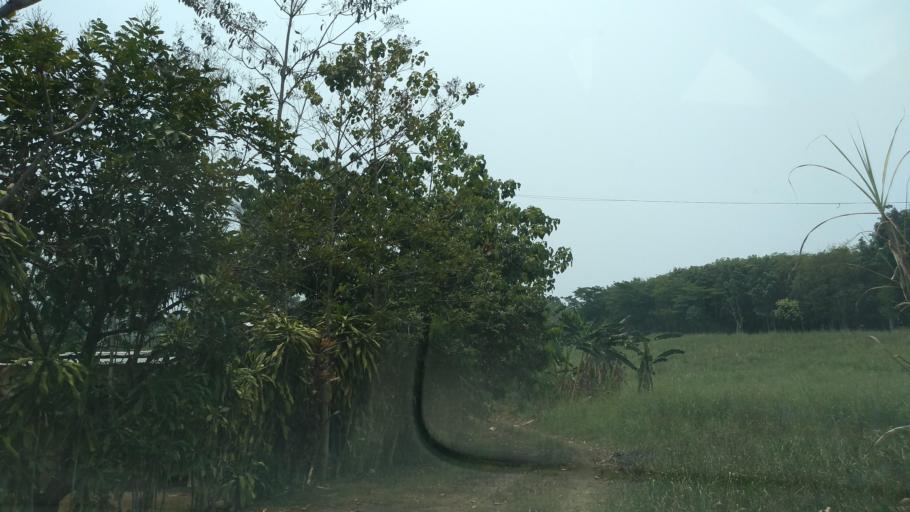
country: MX
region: Puebla
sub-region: San Sebastian Tlacotepec
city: San Martin Mazateopan
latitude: 18.4906
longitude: -96.7801
